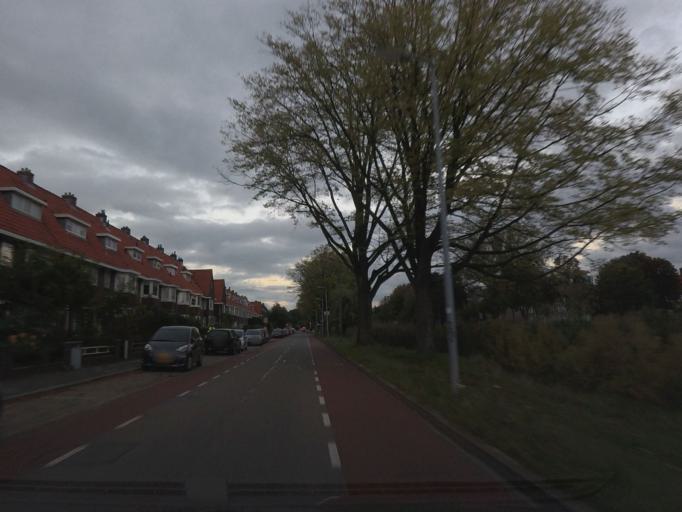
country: NL
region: North Holland
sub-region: Gemeente Alkmaar
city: Alkmaar
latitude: 52.6362
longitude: 4.7316
